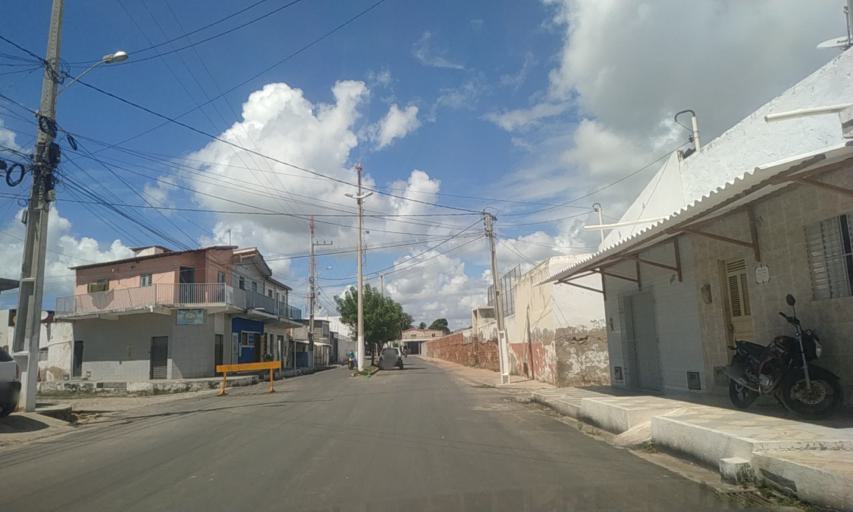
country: BR
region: Rio Grande do Norte
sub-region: Areia Branca
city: Areia Branca
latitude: -4.9518
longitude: -37.1291
